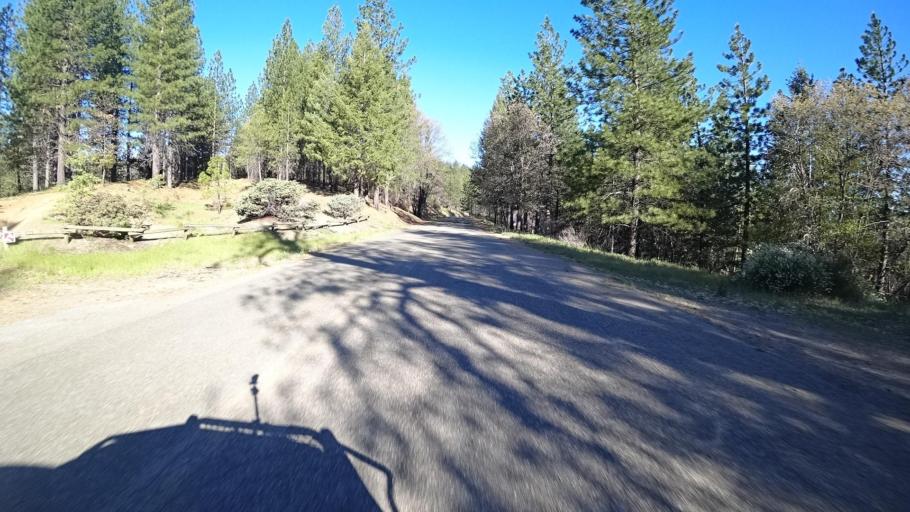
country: US
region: California
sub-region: Lake County
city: Upper Lake
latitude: 39.3125
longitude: -122.9439
